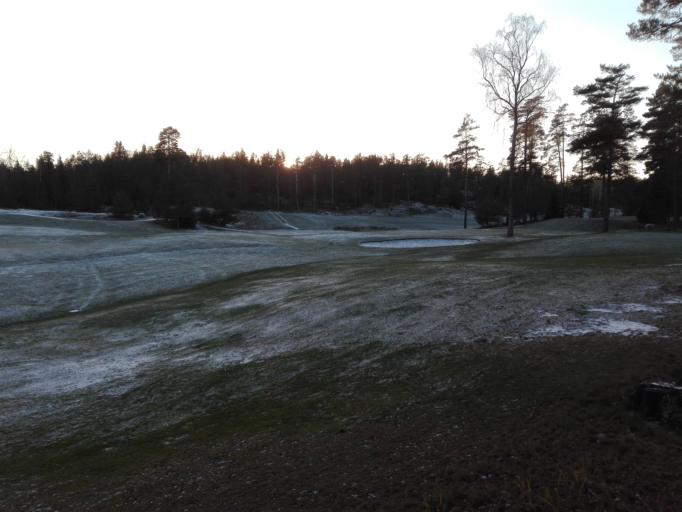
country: SE
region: Stockholm
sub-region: Nacka Kommun
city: Fisksatra
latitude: 59.2860
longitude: 18.2425
